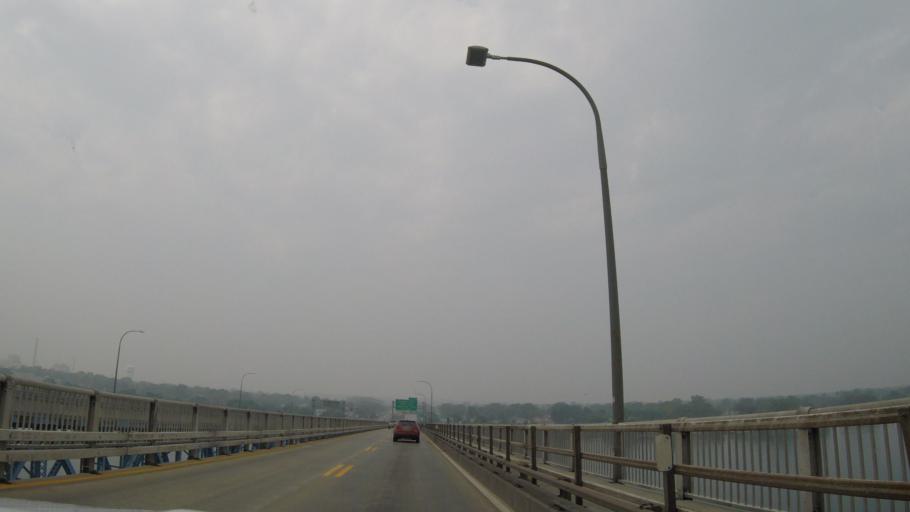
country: US
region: New York
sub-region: Niagara County
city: Niagara Falls
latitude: 43.0697
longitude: -78.9904
